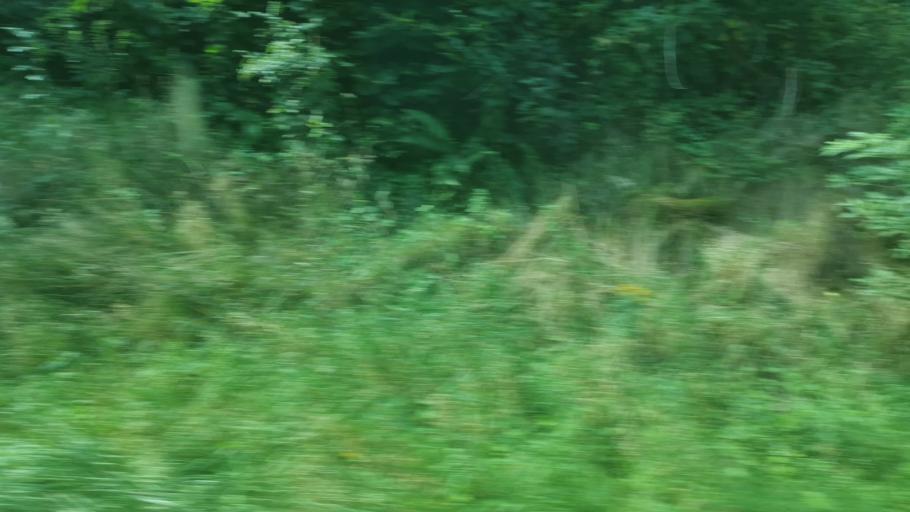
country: DE
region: Bavaria
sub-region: Upper Palatinate
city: Chamerau
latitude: 49.1878
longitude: 12.7328
